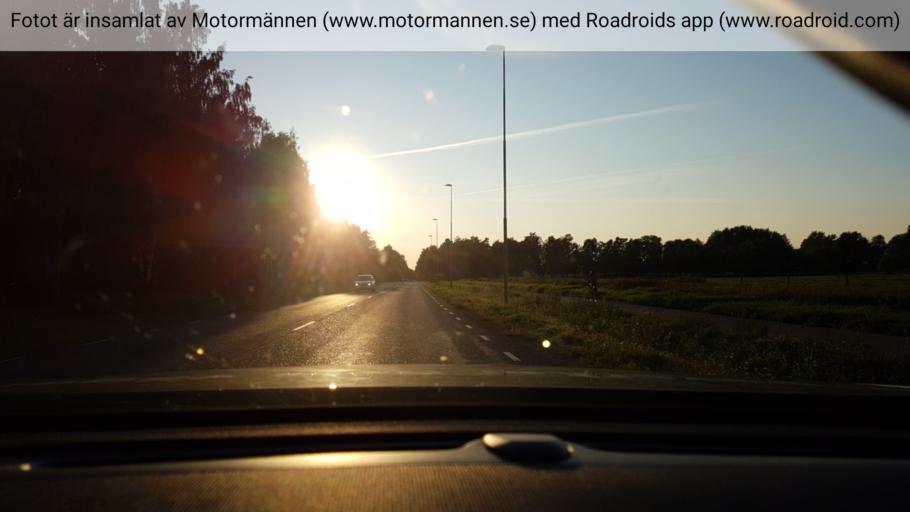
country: SE
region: Halland
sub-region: Halmstads Kommun
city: Mjallby
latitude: 56.6547
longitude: 12.7792
